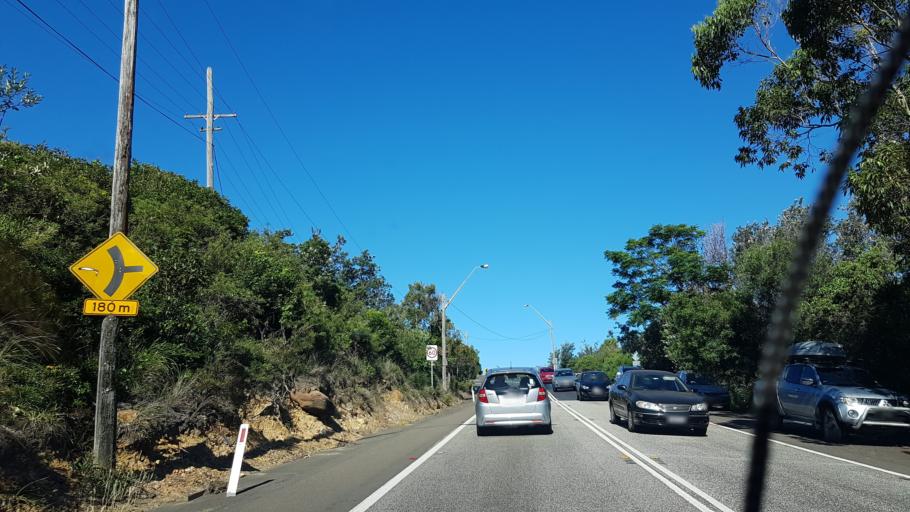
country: AU
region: New South Wales
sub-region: Pittwater
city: Bilgola Beach
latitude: -33.6486
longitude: 151.3249
